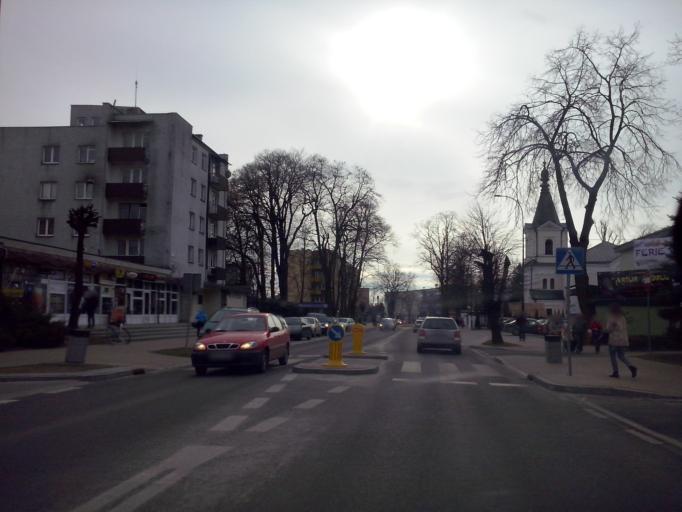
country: PL
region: Lublin Voivodeship
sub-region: Powiat bilgorajski
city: Bilgoraj
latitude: 50.5400
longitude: 22.7216
